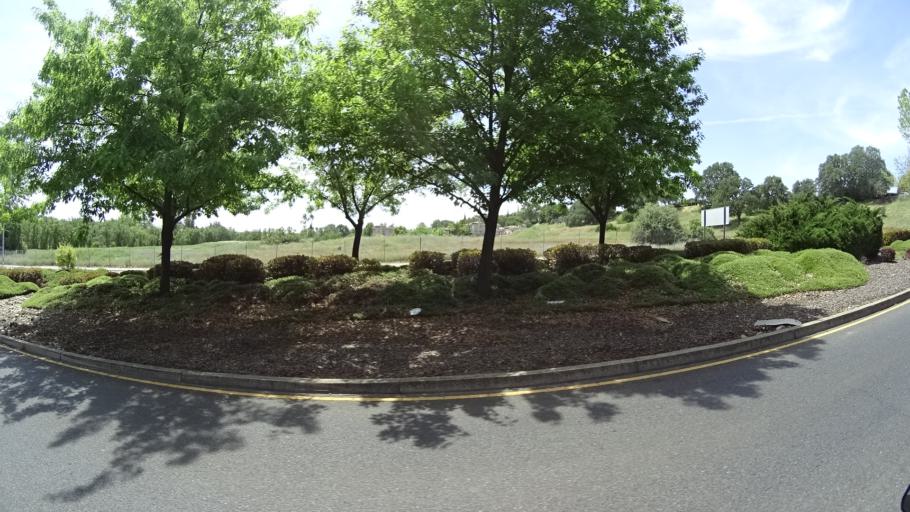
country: US
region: California
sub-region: Placer County
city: Rocklin
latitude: 38.7874
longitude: -121.2538
